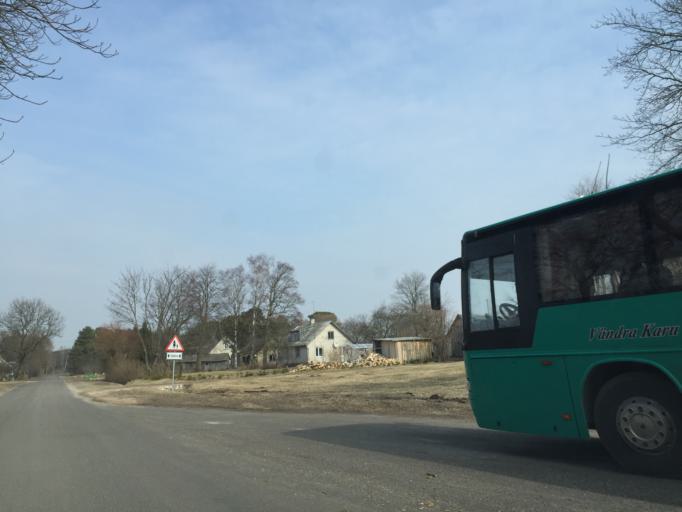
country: LV
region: Salacgrivas
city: Ainazi
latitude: 57.8772
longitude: 24.3624
